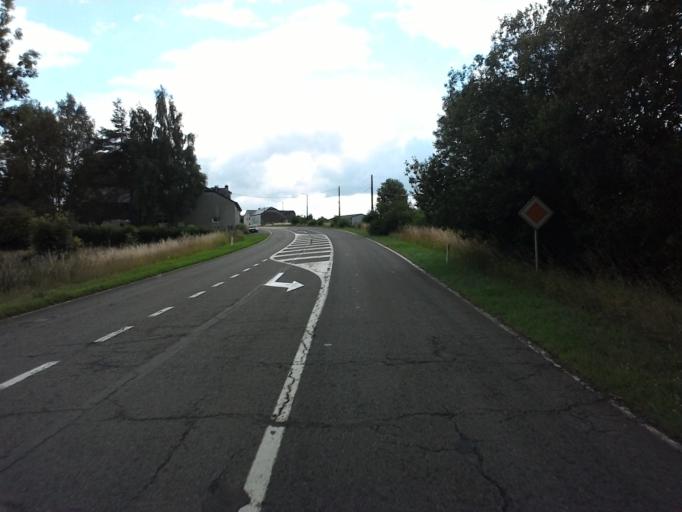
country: BE
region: Wallonia
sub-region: Province du Luxembourg
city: Leglise
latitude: 49.7976
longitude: 5.5627
